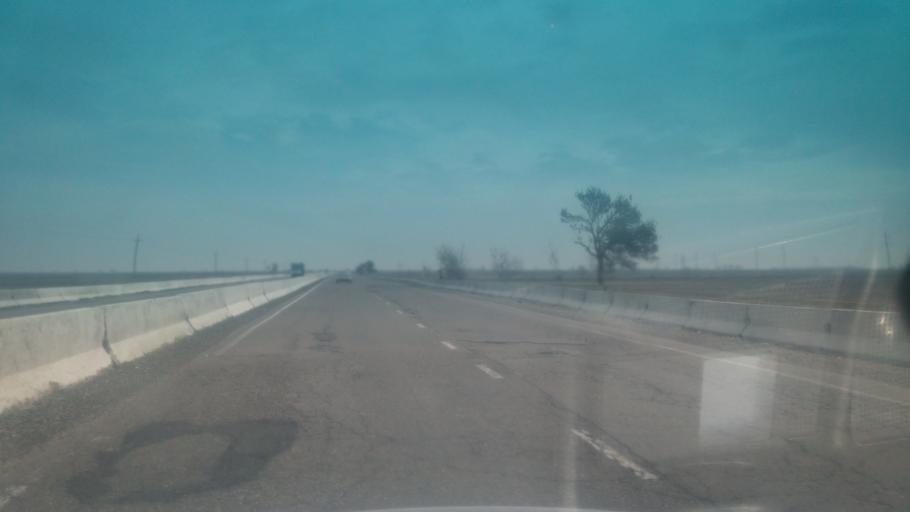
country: KZ
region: Ongtustik Qazaqstan
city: Myrzakent
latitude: 40.5219
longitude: 68.4605
